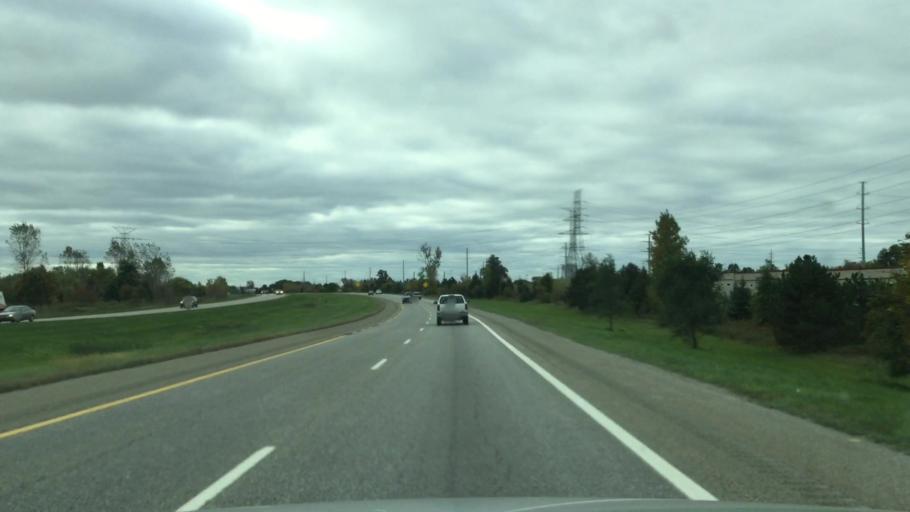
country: US
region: Michigan
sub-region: Macomb County
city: Romeo
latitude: 42.7835
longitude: -83.0077
